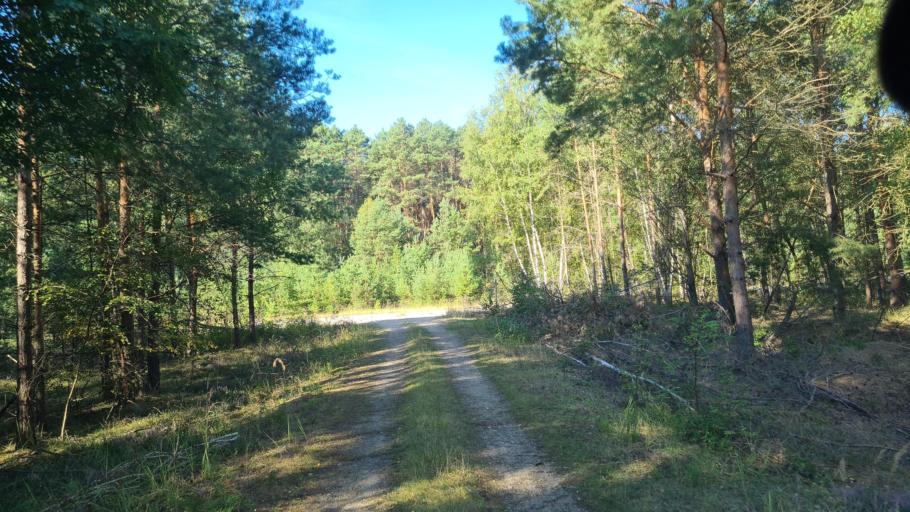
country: DE
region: Brandenburg
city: Schonborn
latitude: 51.6380
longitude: 13.5134
